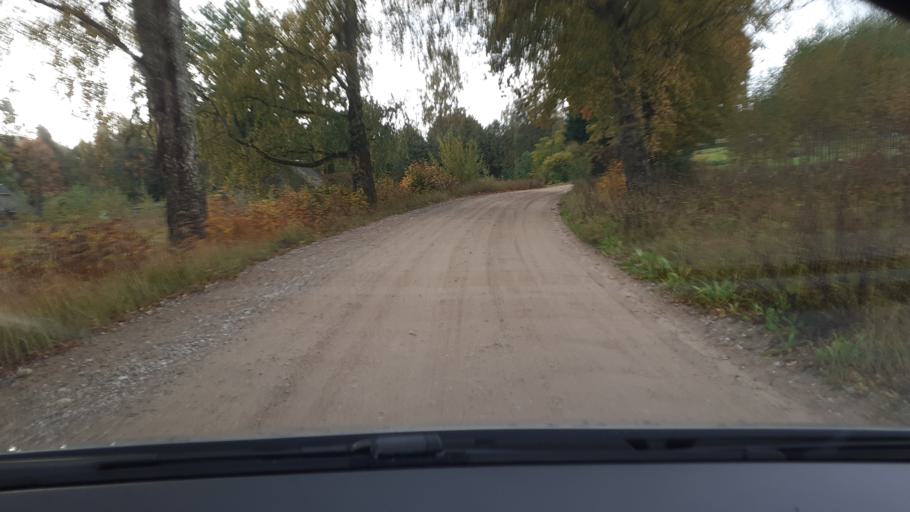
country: LV
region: Kuldigas Rajons
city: Kuldiga
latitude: 57.0295
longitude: 21.9154
